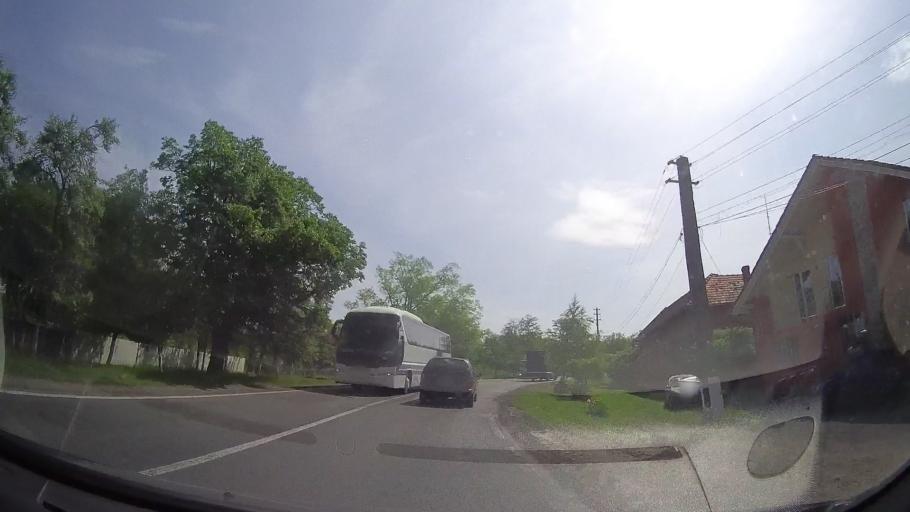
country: RO
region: Timis
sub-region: Comuna Curtea
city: Curtea
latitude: 45.8496
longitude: 22.3185
